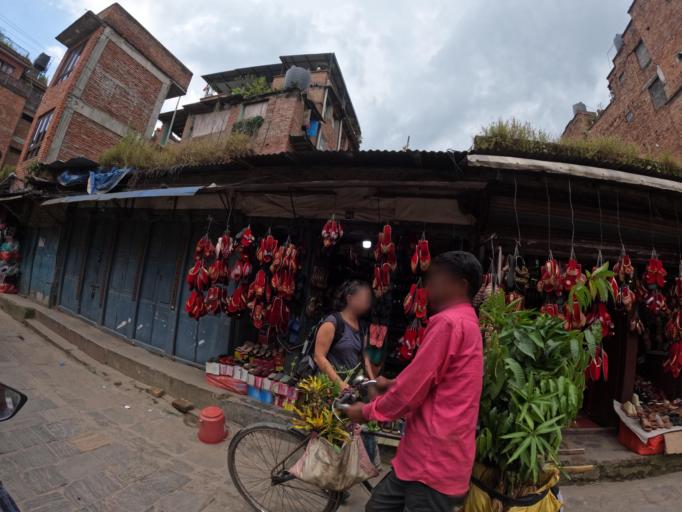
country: NP
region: Central Region
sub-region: Bagmati Zone
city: Bhaktapur
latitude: 27.6703
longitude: 85.4275
